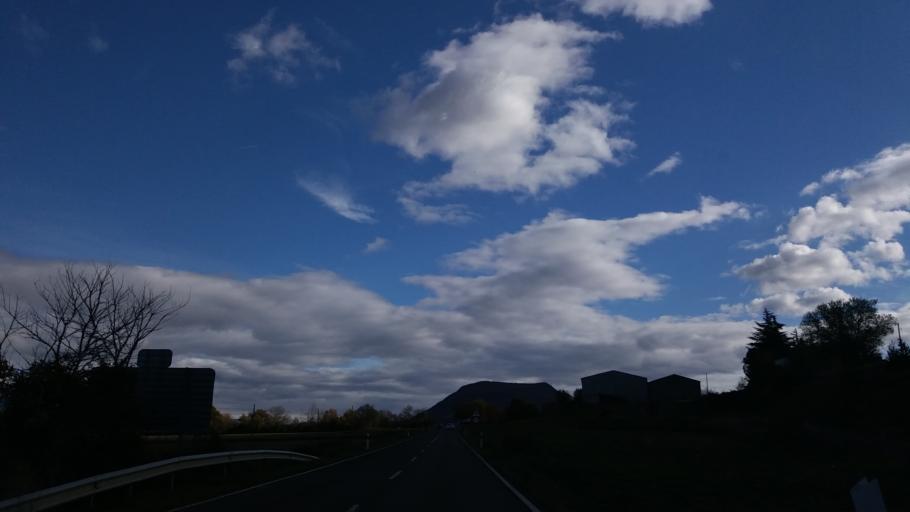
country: ES
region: Aragon
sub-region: Provincia de Huesca
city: Santa Cruz de la Seros
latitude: 42.5573
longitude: -0.7070
